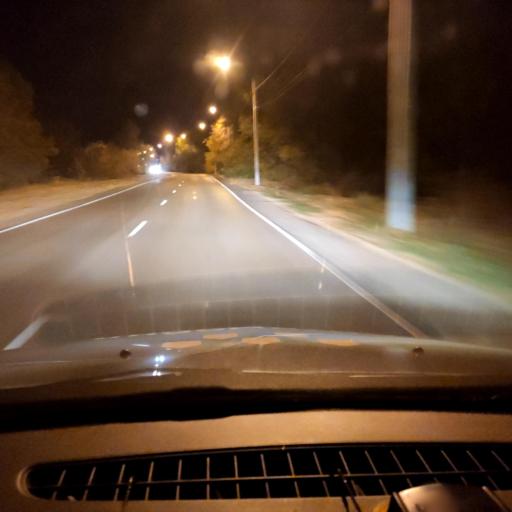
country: RU
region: Voronezj
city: Shilovo
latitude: 51.6058
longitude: 39.0403
